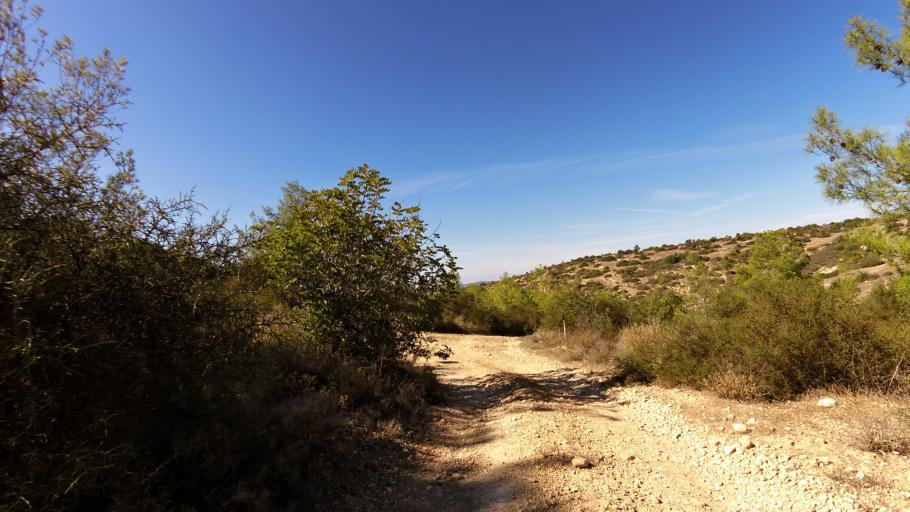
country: CY
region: Pafos
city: Polis
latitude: 35.0156
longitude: 32.4821
